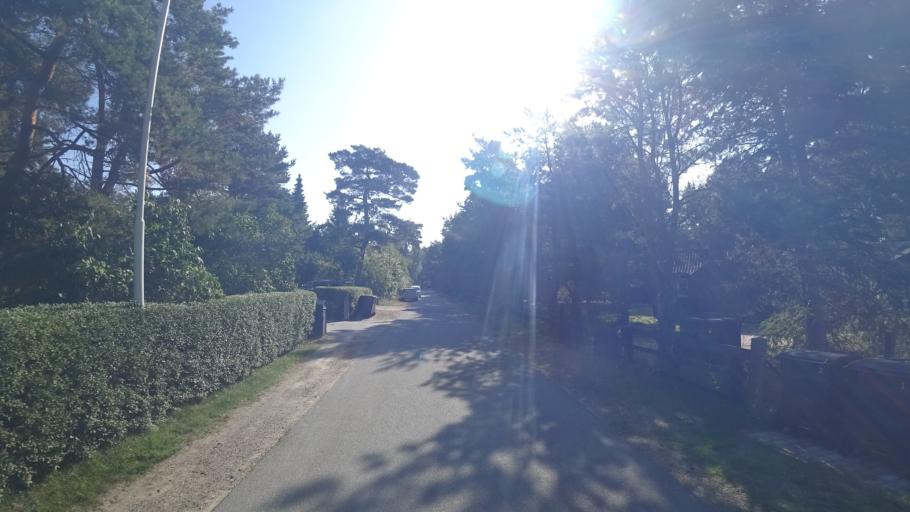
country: SE
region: Skane
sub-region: Kristianstads Kommun
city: Ahus
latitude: 55.9187
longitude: 14.3033
